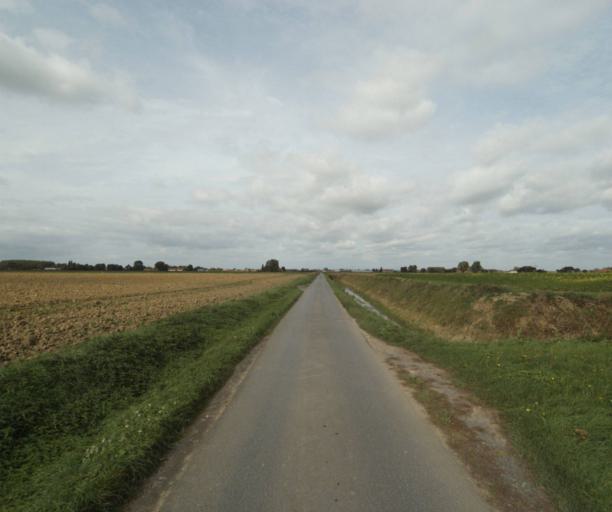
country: FR
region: Nord-Pas-de-Calais
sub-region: Departement du Nord
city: Bois-Grenier
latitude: 50.6407
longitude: 2.8640
